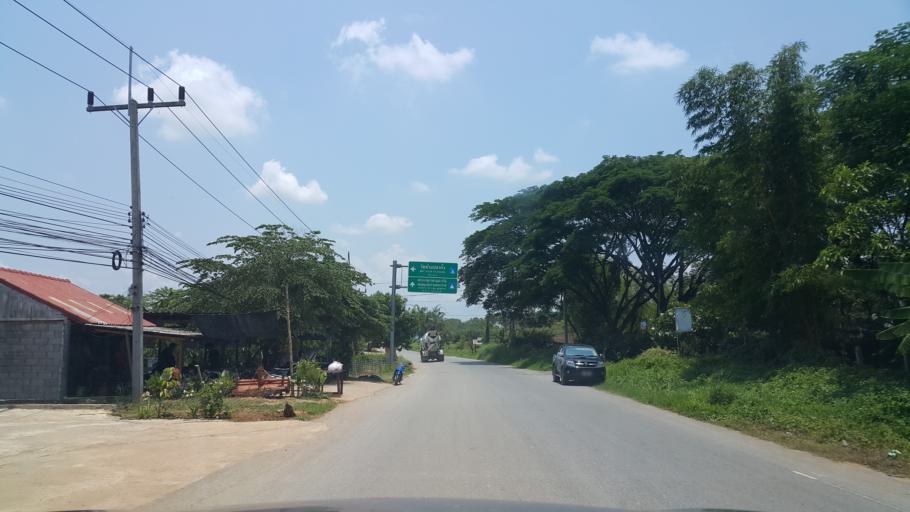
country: TH
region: Chiang Rai
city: Chiang Rai
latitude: 19.9421
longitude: 99.8048
